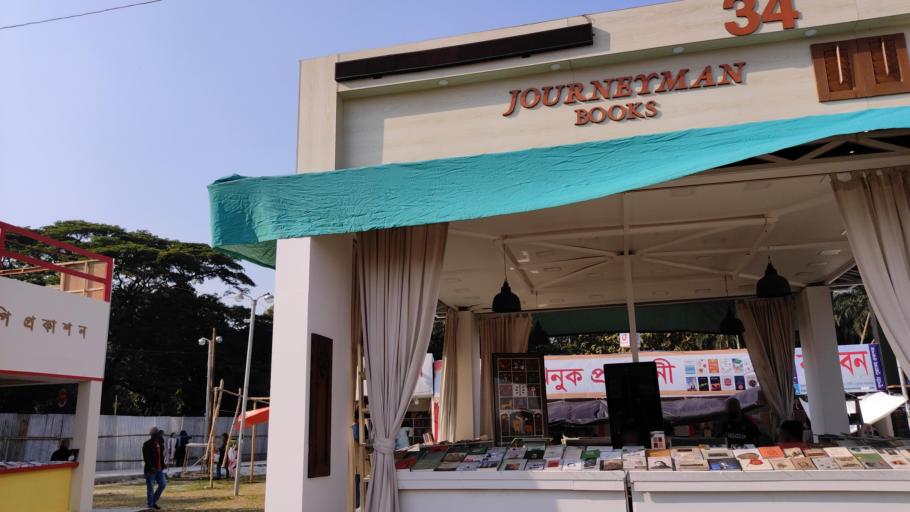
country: BD
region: Dhaka
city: Azimpur
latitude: 23.7331
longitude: 90.3977
